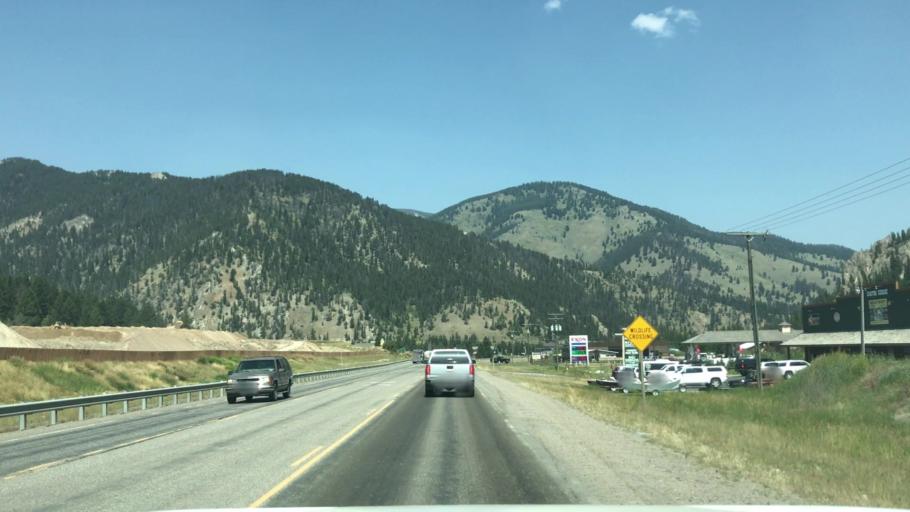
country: US
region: Montana
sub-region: Gallatin County
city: Big Sky
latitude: 45.2576
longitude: -111.2544
